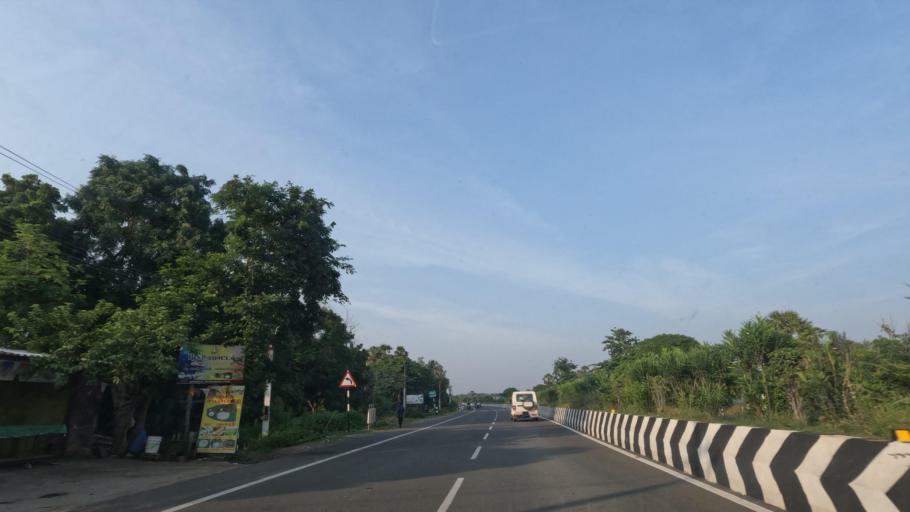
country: IN
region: Tamil Nadu
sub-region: Kancheepuram
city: Mamallapuram
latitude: 12.6570
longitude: 80.2079
